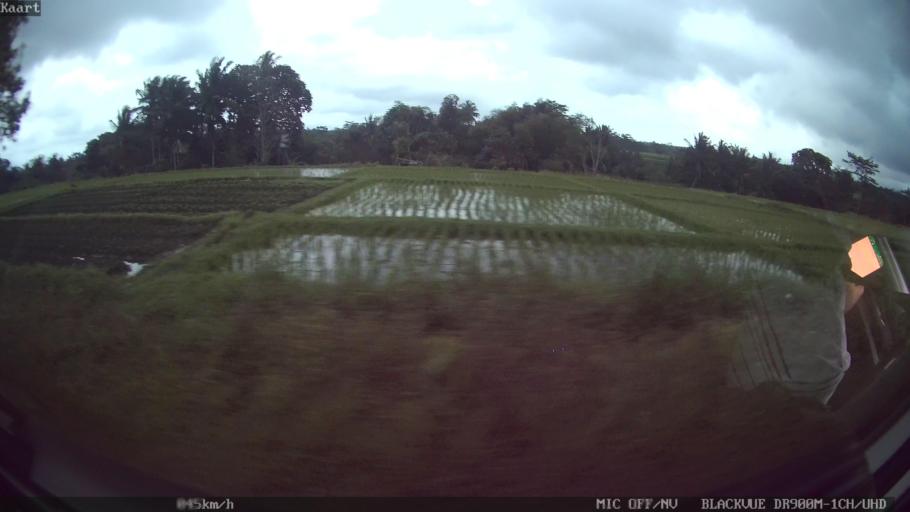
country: ID
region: Bali
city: Banjar Badung Tengah
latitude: -8.5146
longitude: 115.1967
